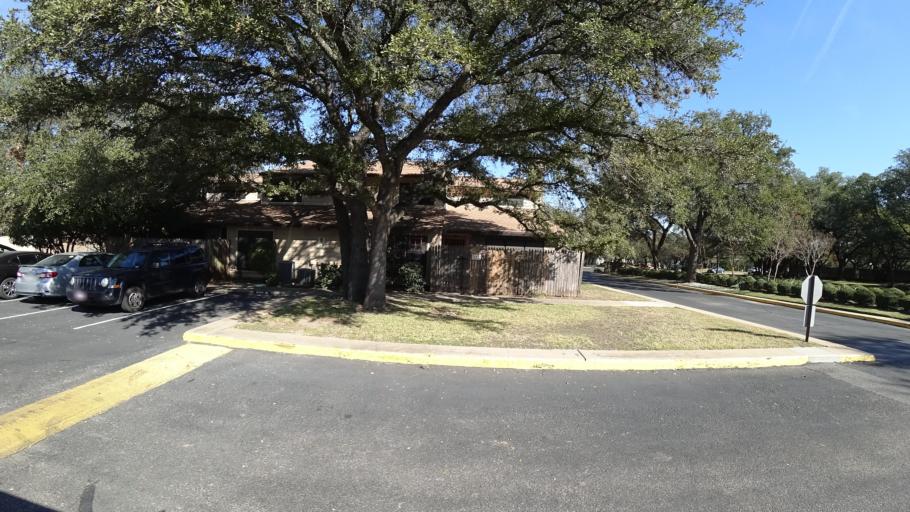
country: US
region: Texas
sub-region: Williamson County
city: Jollyville
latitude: 30.3758
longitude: -97.7577
